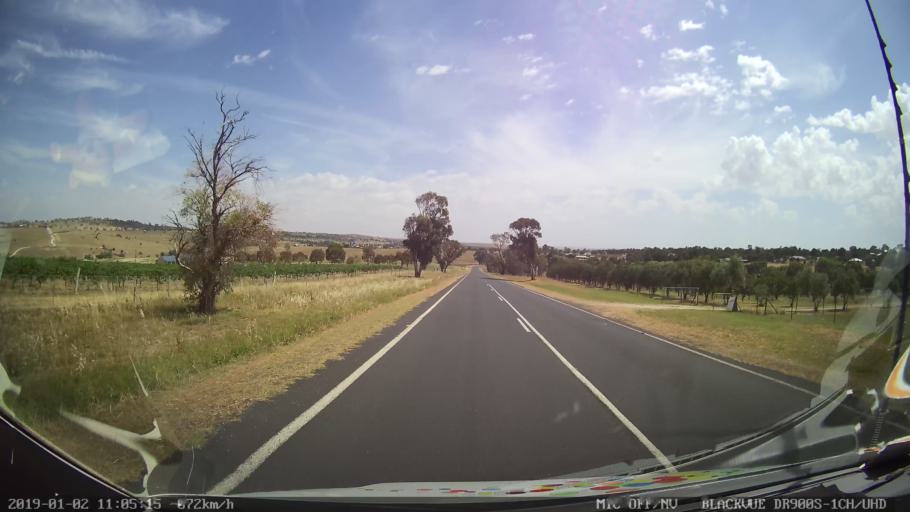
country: AU
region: New South Wales
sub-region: Young
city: Young
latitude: -34.5670
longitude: 148.3541
